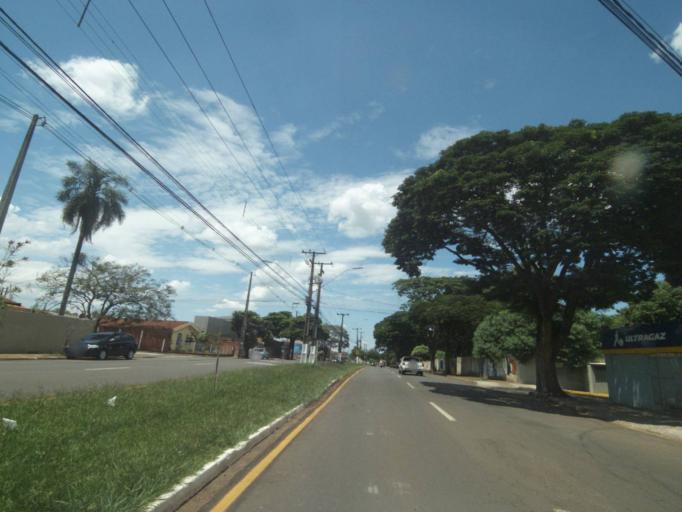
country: BR
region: Parana
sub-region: Londrina
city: Londrina
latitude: -23.3075
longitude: -51.2012
